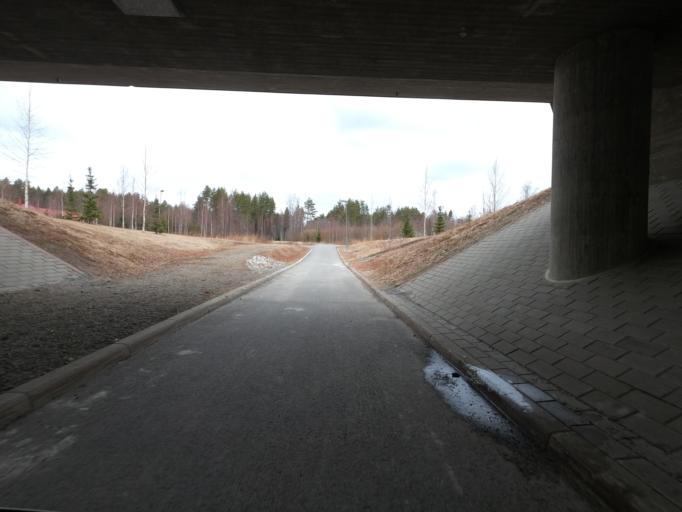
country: FI
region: North Karelia
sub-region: Joensuu
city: Joensuu
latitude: 62.5712
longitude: 29.8130
